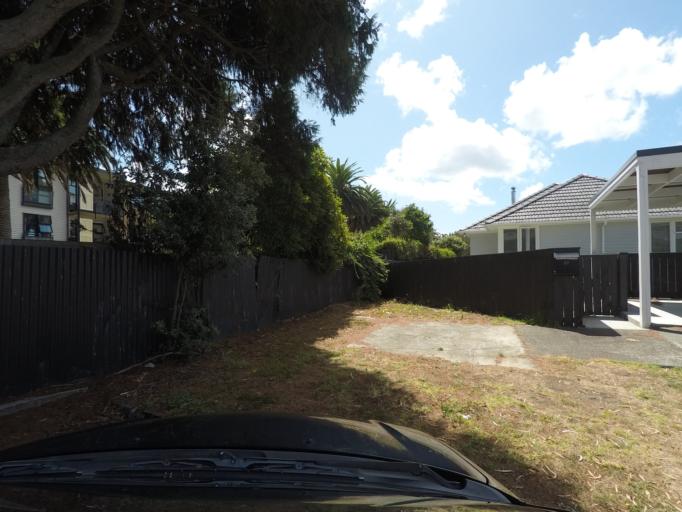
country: NZ
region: Auckland
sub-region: Auckland
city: Rosebank
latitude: -36.8649
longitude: 174.7004
